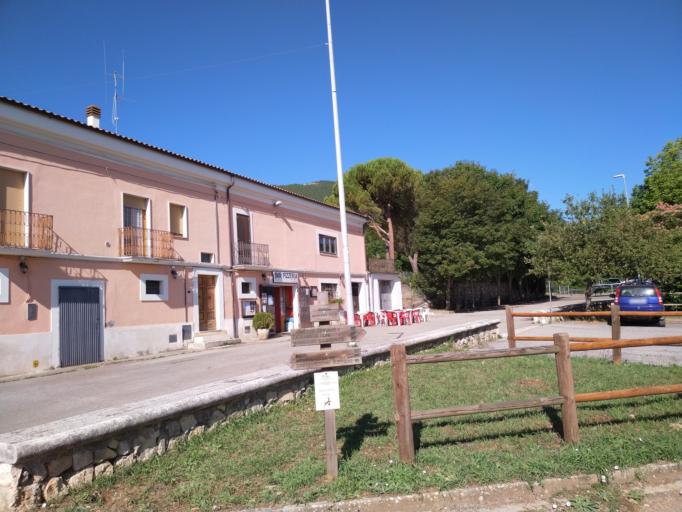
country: IT
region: Abruzzo
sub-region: Provincia dell' Aquila
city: Secinaro
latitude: 42.1798
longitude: 13.6696
